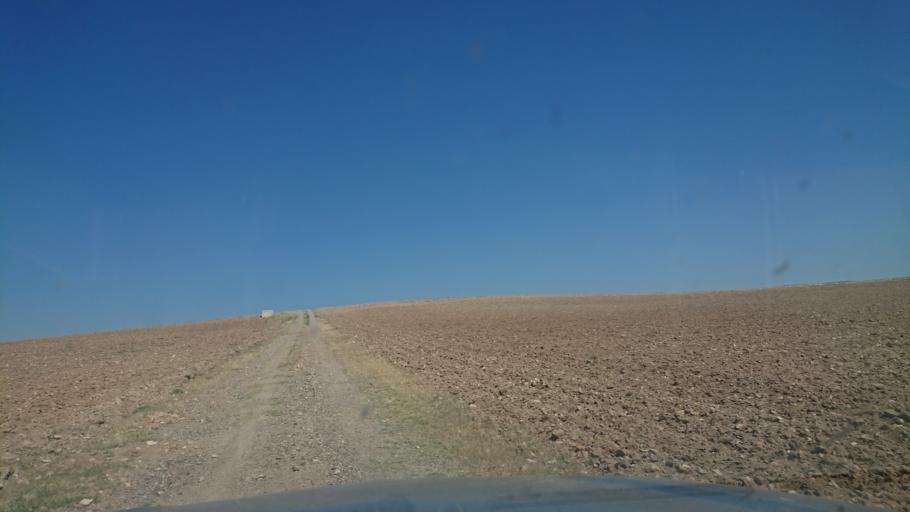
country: TR
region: Aksaray
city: Sariyahsi
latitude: 39.0540
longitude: 33.8888
